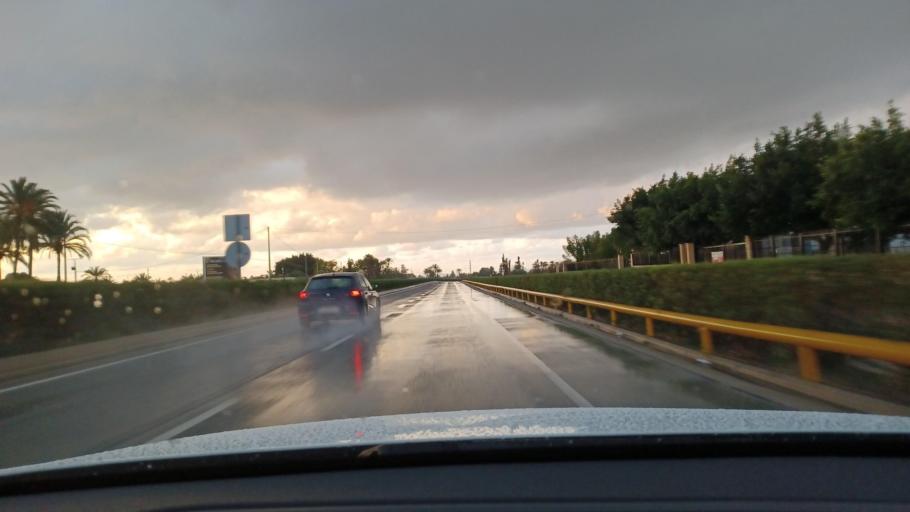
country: ES
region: Valencia
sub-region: Provincia de Alicante
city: Elche
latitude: 38.2382
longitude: -0.7003
